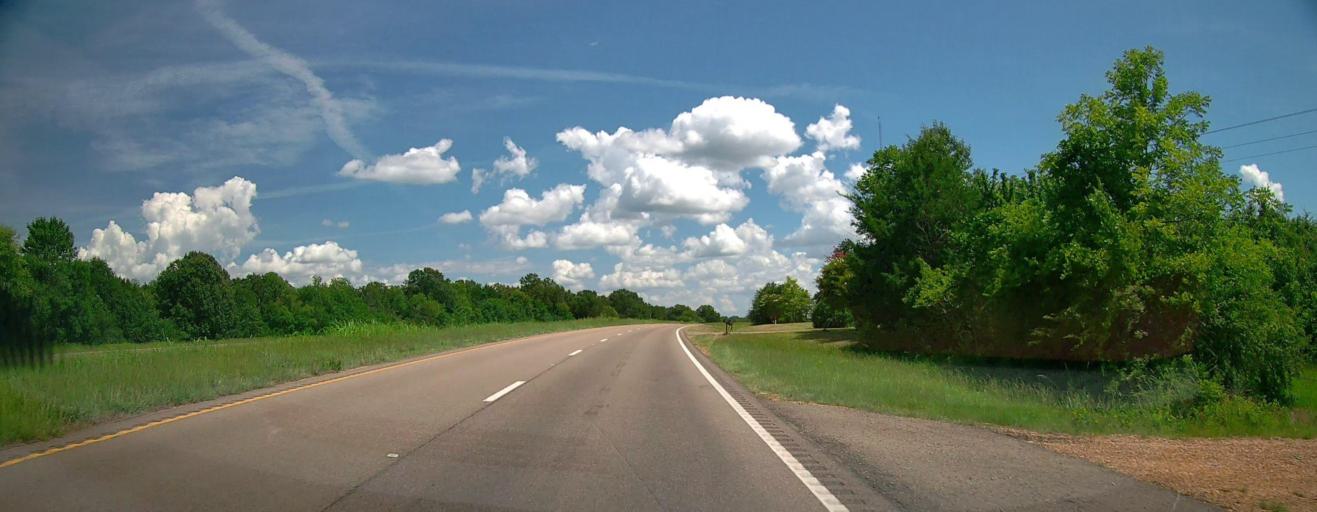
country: US
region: Mississippi
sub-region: Monroe County
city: Amory
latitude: 33.9544
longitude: -88.6058
